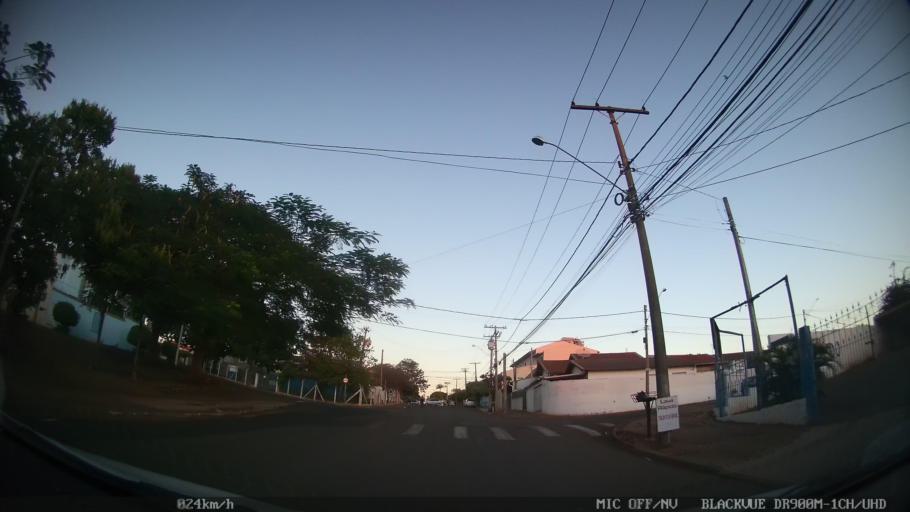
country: BR
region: Sao Paulo
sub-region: Santa Barbara D'Oeste
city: Santa Barbara d'Oeste
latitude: -22.7598
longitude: -47.4033
